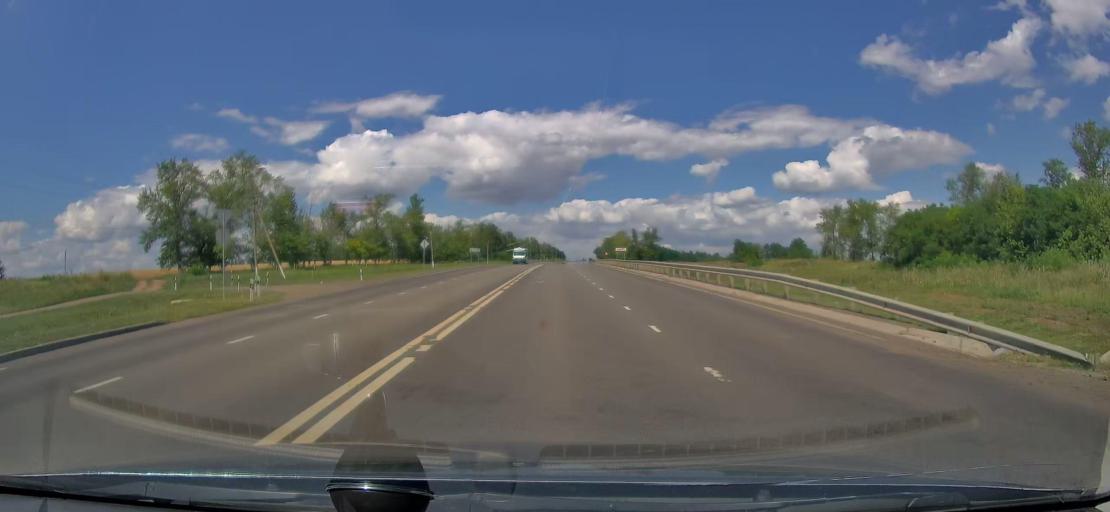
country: RU
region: Kursk
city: Zolotukhino
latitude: 51.9519
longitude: 36.3046
